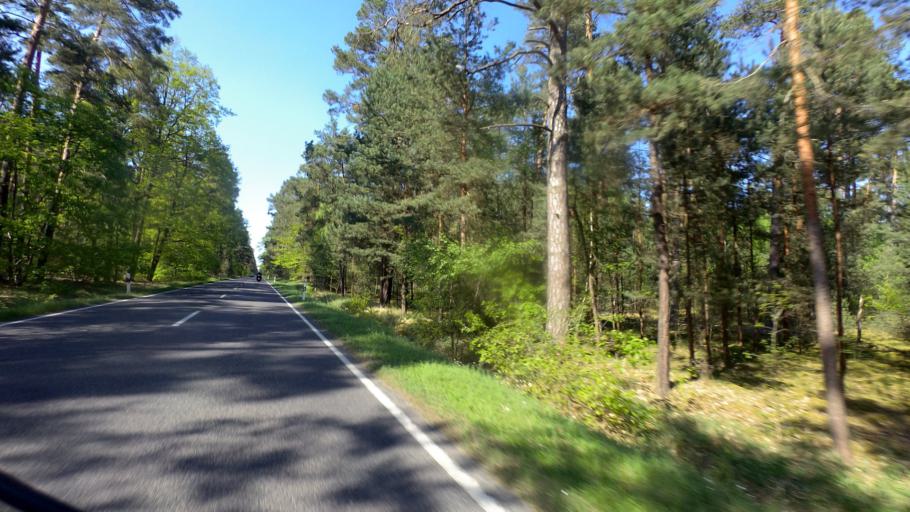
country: DE
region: Brandenburg
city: Gross Koris
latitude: 52.1995
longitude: 13.6941
